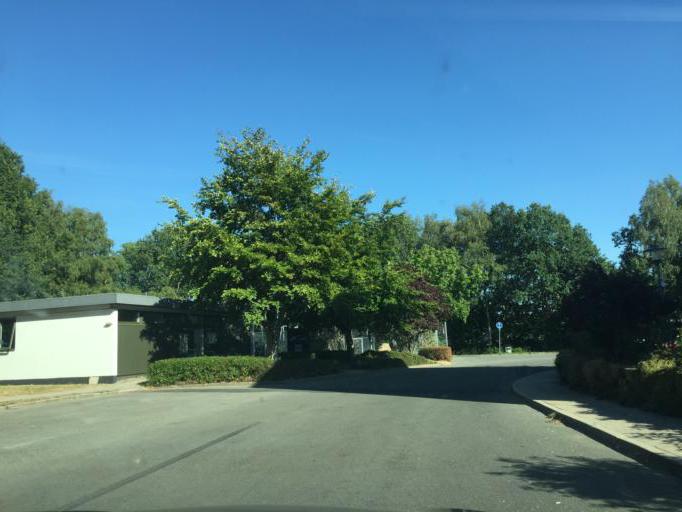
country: DK
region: South Denmark
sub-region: Odense Kommune
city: Seden
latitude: 55.4088
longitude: 10.4204
